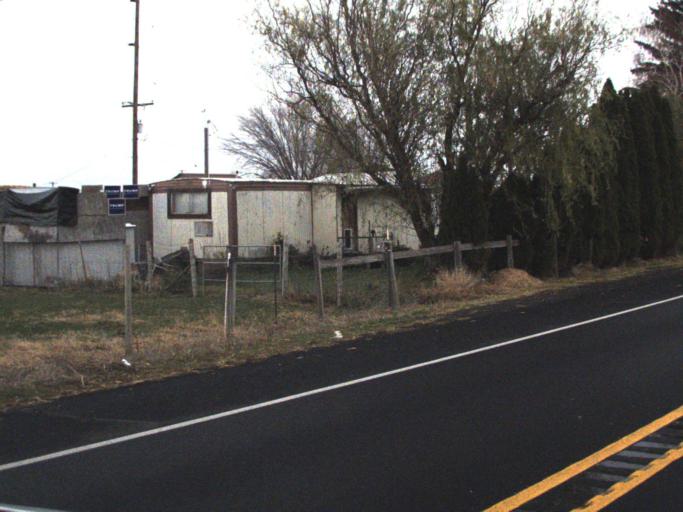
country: US
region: Washington
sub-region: Walla Walla County
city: Garrett
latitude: 46.0565
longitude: -118.5880
